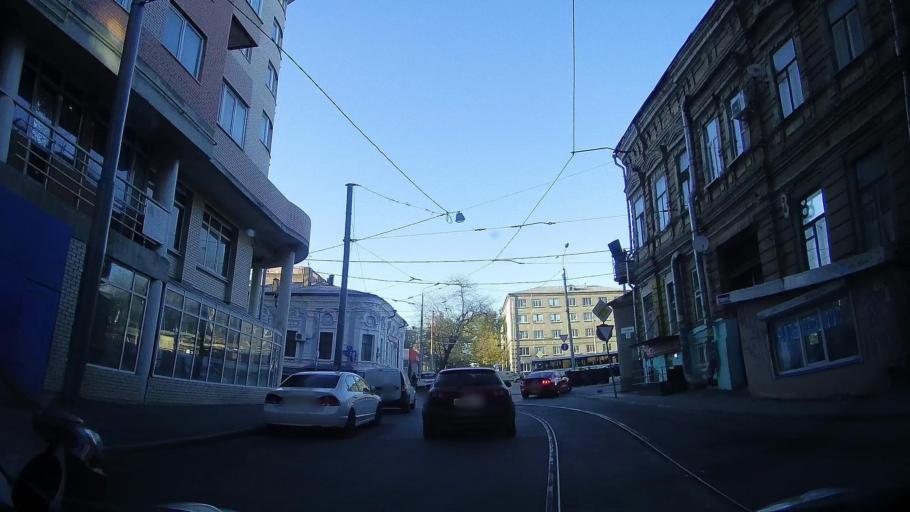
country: RU
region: Rostov
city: Rostov-na-Donu
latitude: 47.2161
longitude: 39.7066
